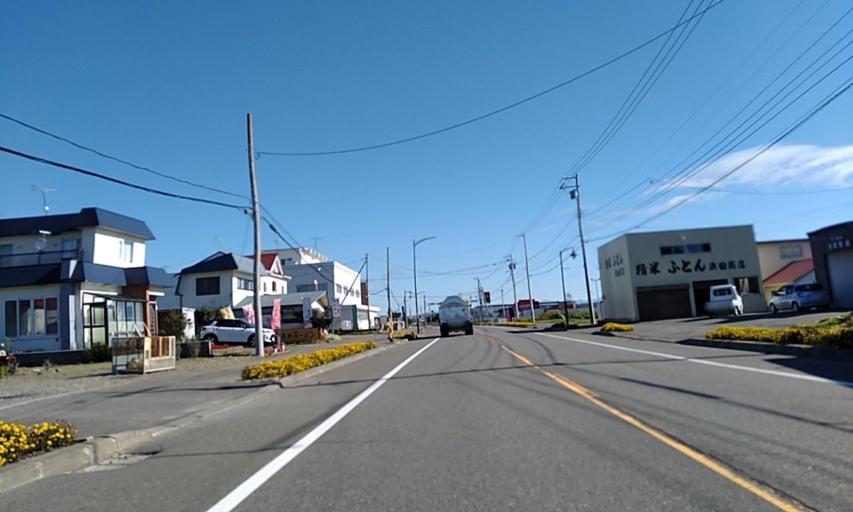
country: JP
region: Hokkaido
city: Shizunai-furukawacho
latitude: 42.5218
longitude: 142.0363
